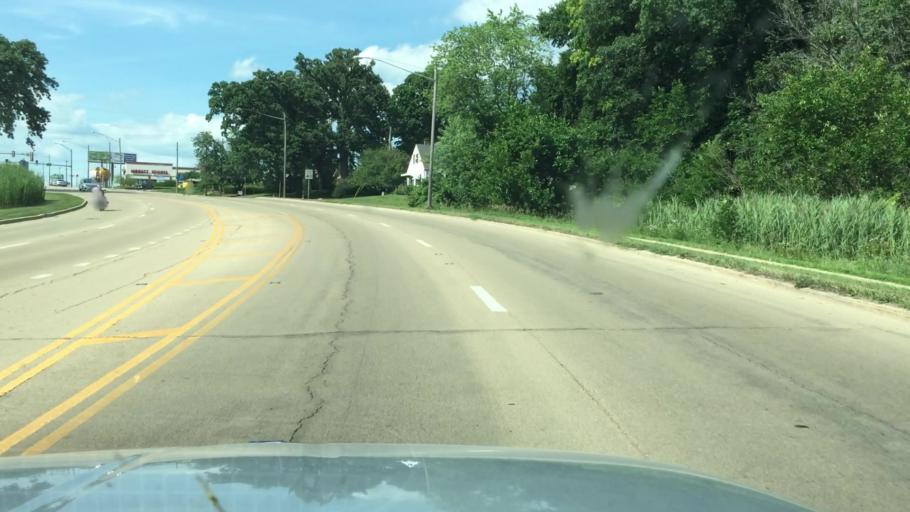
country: US
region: Illinois
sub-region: LaSalle County
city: Ottawa
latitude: 41.3678
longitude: -88.8356
